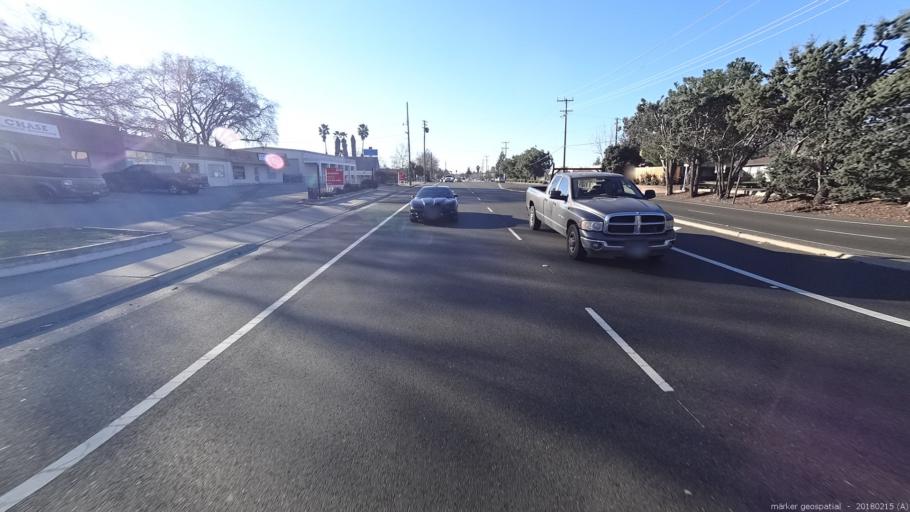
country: US
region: California
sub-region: Sacramento County
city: Foothill Farms
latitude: 38.6702
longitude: -121.3366
